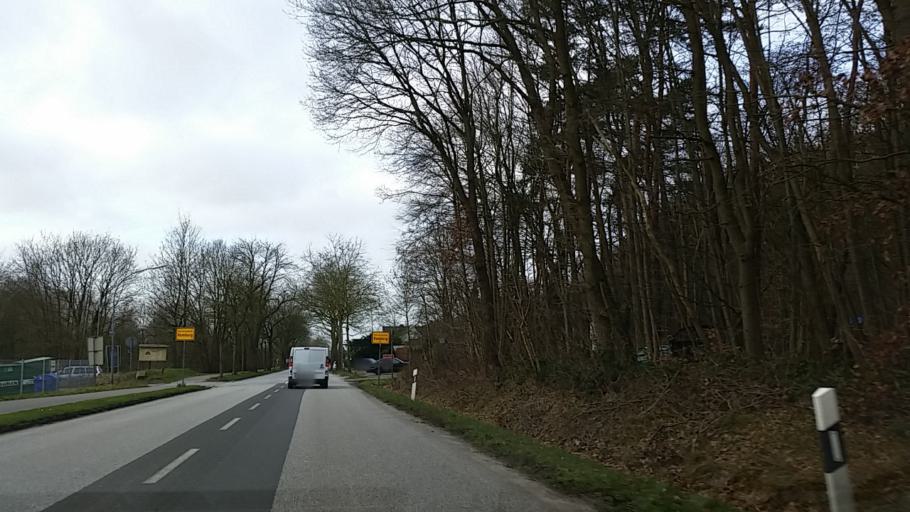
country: DE
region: Schleswig-Holstein
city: Bornsen
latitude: 53.4714
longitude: 10.2666
